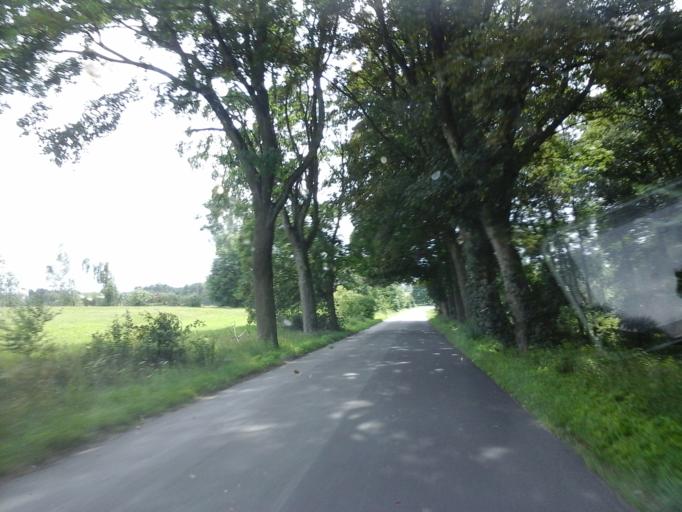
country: PL
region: Lubusz
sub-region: Powiat strzelecko-drezdenecki
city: Dobiegniew
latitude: 53.0564
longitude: 15.7581
